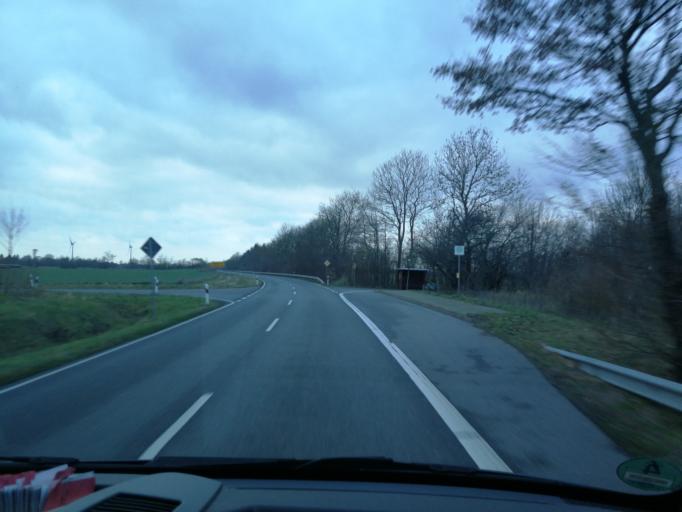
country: DE
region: Schleswig-Holstein
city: Boxlund
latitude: 54.8560
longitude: 9.1758
